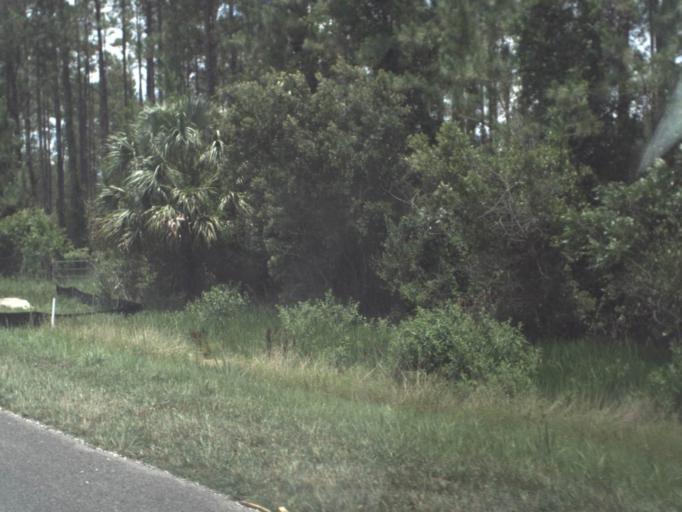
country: US
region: Florida
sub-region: Putnam County
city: Palatka
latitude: 29.5093
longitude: -81.7490
